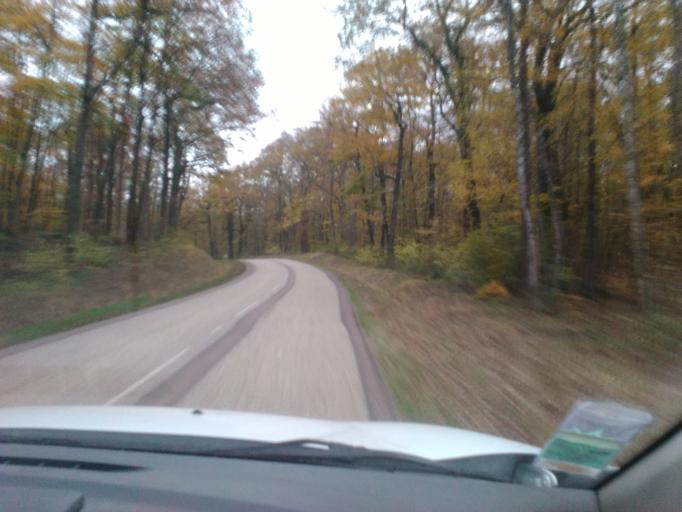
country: FR
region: Lorraine
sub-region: Departement des Vosges
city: Darnieulles
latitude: 48.2351
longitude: 6.2895
